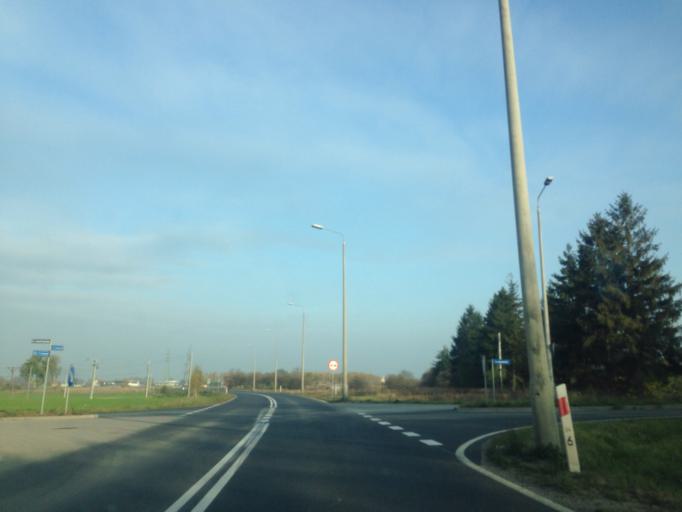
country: PL
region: Kujawsko-Pomorskie
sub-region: Powiat wabrzeski
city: Wabrzezno
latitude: 53.2640
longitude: 18.9554
